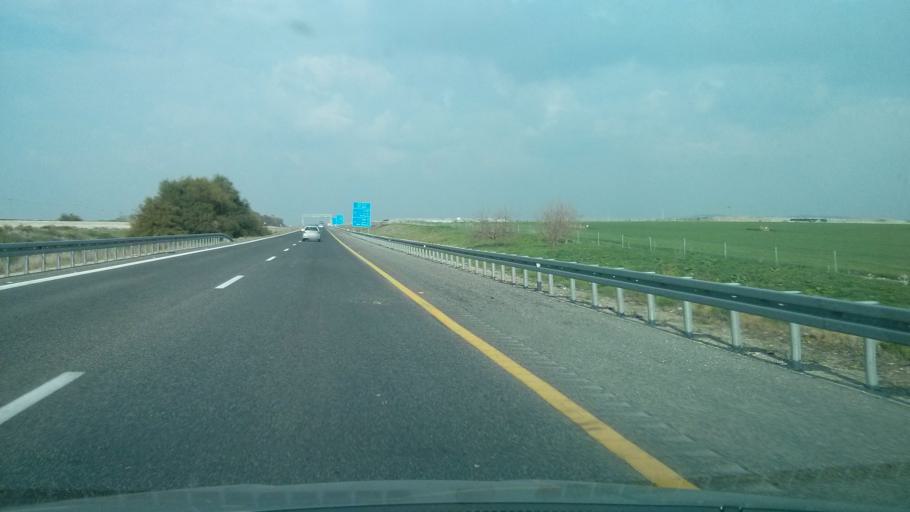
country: IL
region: Central District
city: Mazkeret Batya
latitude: 31.8120
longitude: 34.8386
